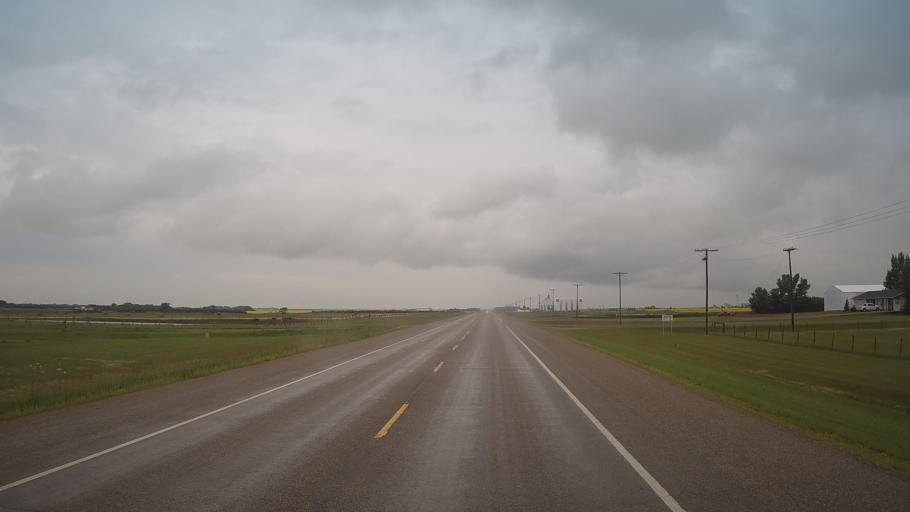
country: CA
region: Saskatchewan
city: Wilkie
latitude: 52.4057
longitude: -108.7363
